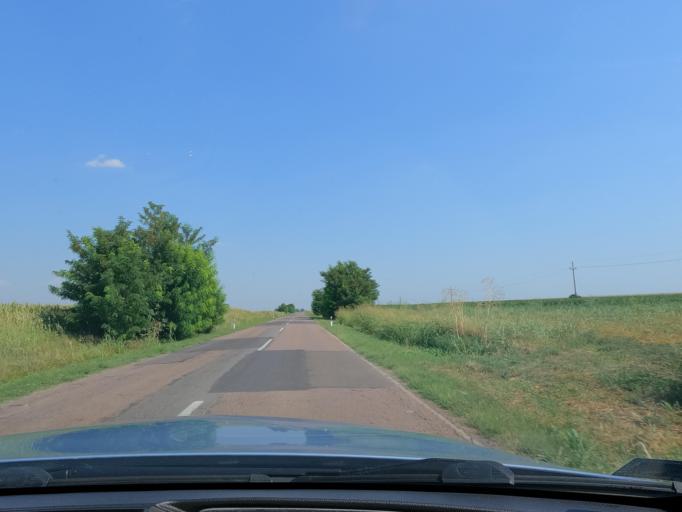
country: RS
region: Autonomna Pokrajina Vojvodina
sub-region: Severnobacki Okrug
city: Mali Igos
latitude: 45.7588
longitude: 19.7643
